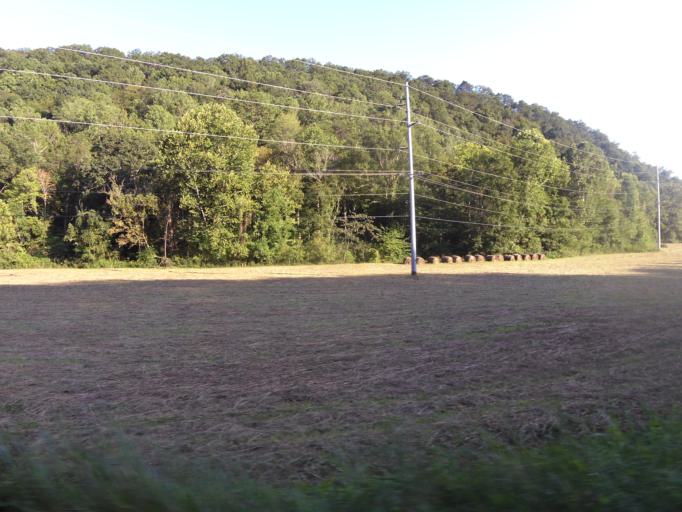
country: US
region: Tennessee
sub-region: Union County
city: Condon
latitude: 36.2083
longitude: -83.8288
